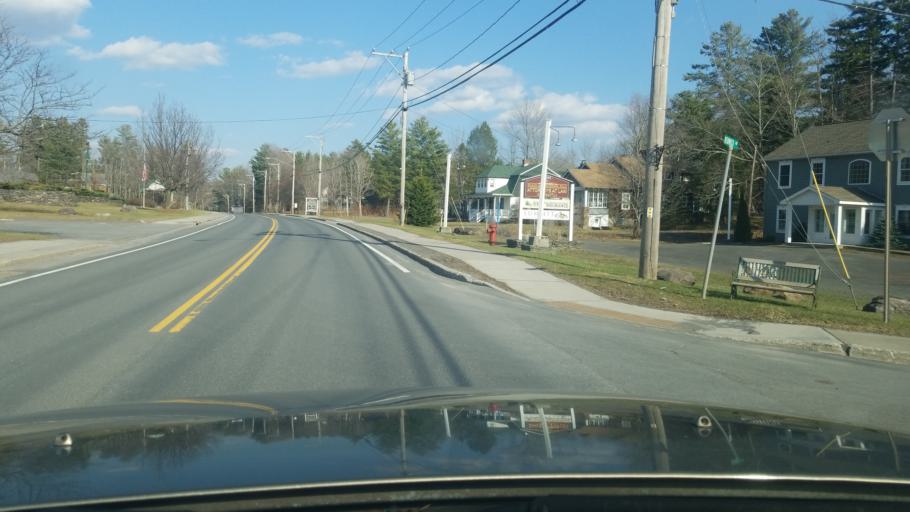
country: US
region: New York
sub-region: Ulster County
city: Manorville
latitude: 42.1954
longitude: -74.1427
